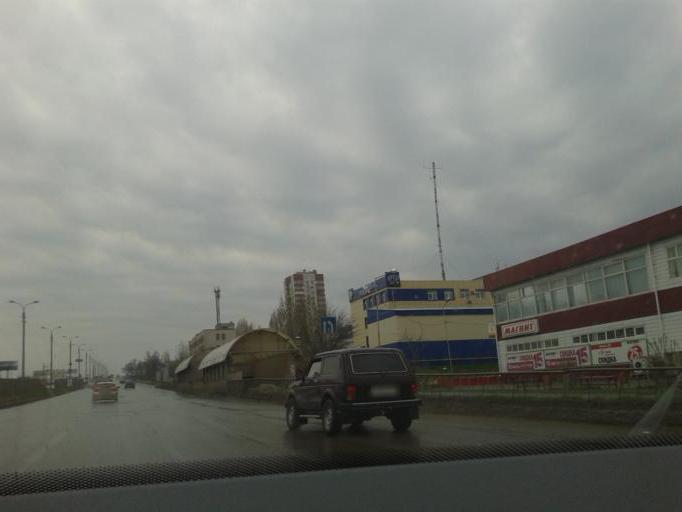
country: RU
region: Volgograd
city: Volgograd
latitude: 48.7574
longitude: 44.4934
